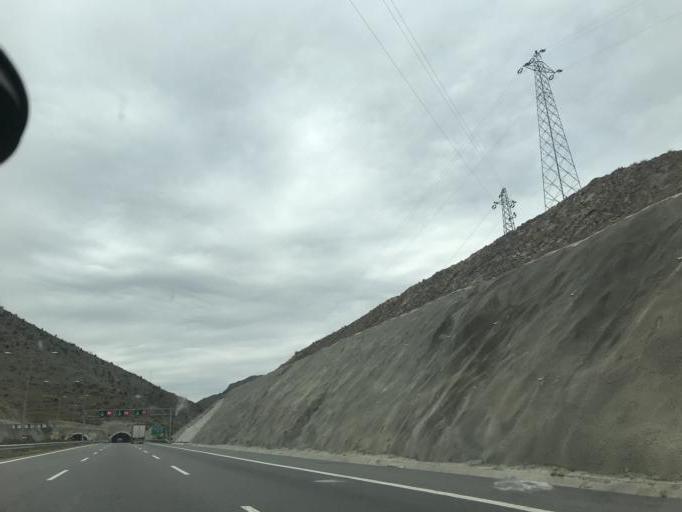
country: TR
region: Nigde
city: Ciftehan
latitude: 37.5703
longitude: 34.7543
